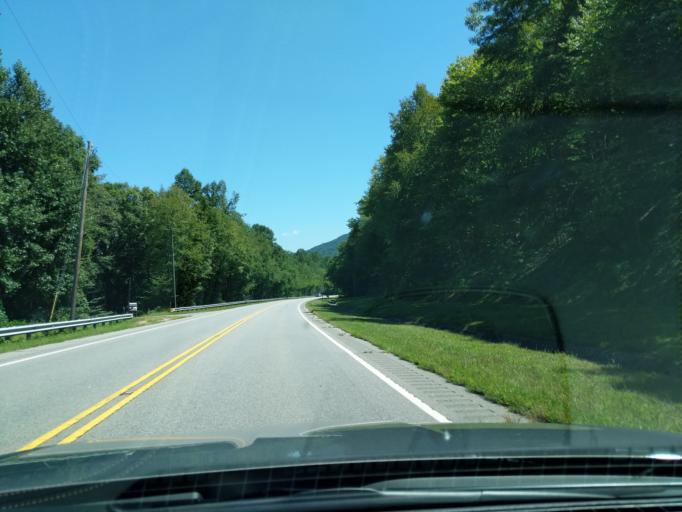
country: US
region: North Carolina
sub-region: Macon County
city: Franklin
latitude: 35.1380
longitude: -83.5012
